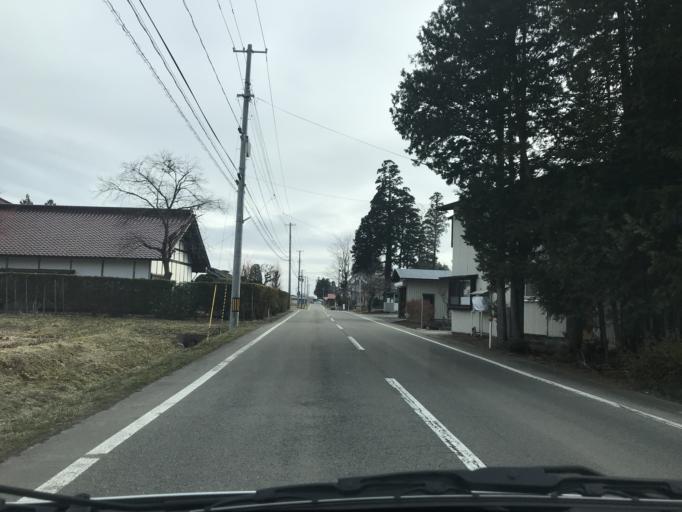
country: JP
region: Iwate
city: Hanamaki
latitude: 39.3489
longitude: 141.0597
